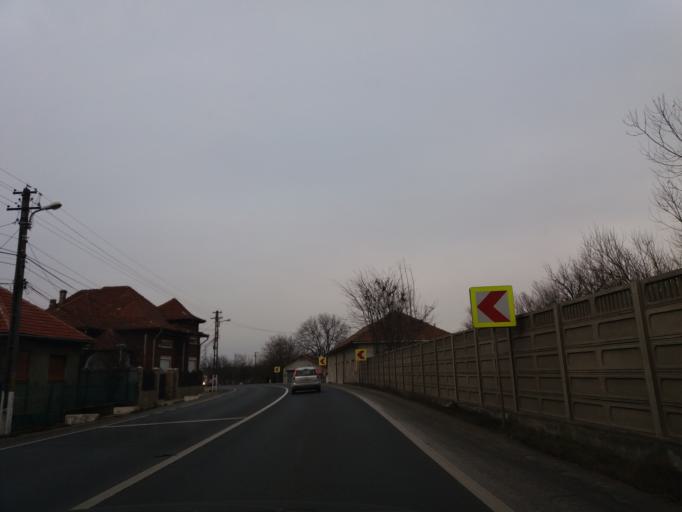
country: RO
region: Hunedoara
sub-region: Comuna Bacia
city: Bacia
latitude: 45.7758
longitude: 23.0019
